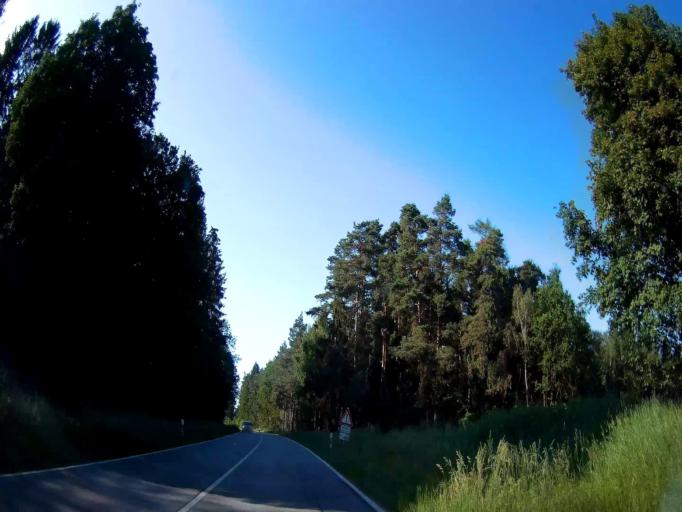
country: DE
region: Bavaria
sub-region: Lower Bavaria
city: Malgersdorf
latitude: 48.5020
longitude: 12.7432
